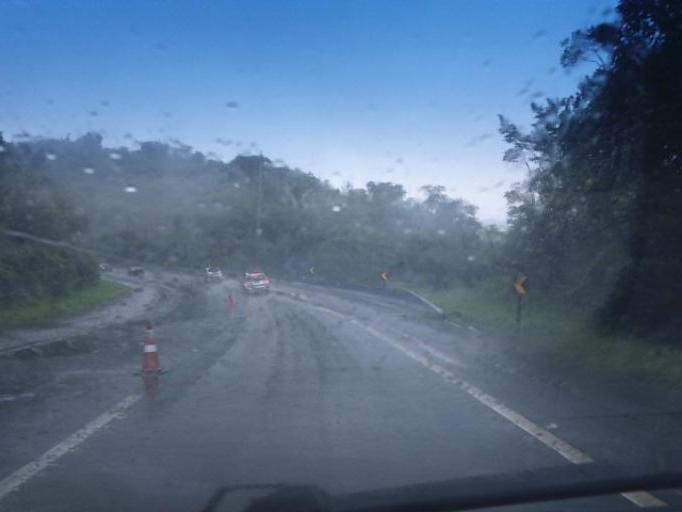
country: BR
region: Parana
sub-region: Antonina
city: Antonina
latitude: -25.1051
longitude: -48.7174
